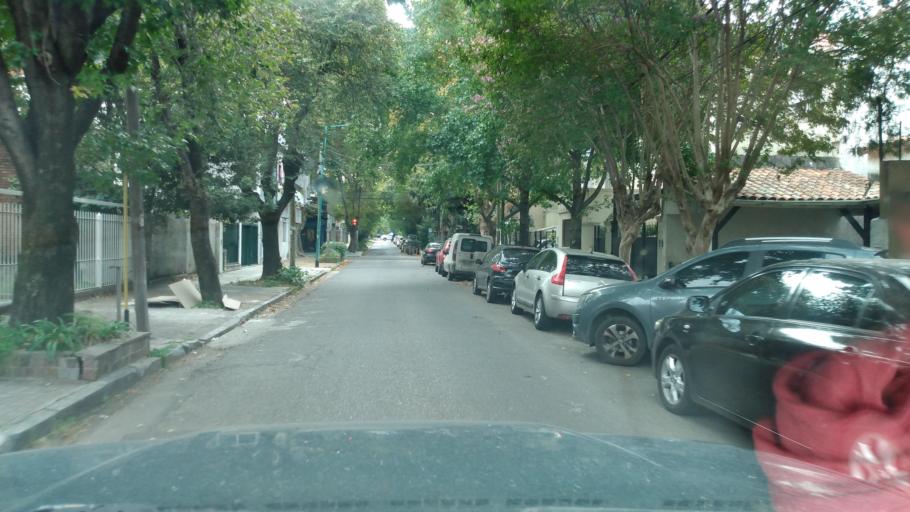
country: AR
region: Buenos Aires
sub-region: Partido de Vicente Lopez
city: Olivos
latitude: -34.5160
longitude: -58.4939
